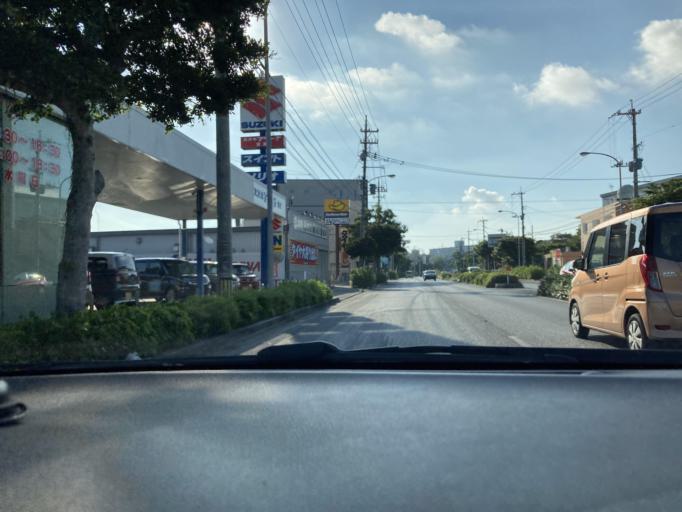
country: JP
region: Okinawa
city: Naha-shi
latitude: 26.2403
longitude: 127.6921
